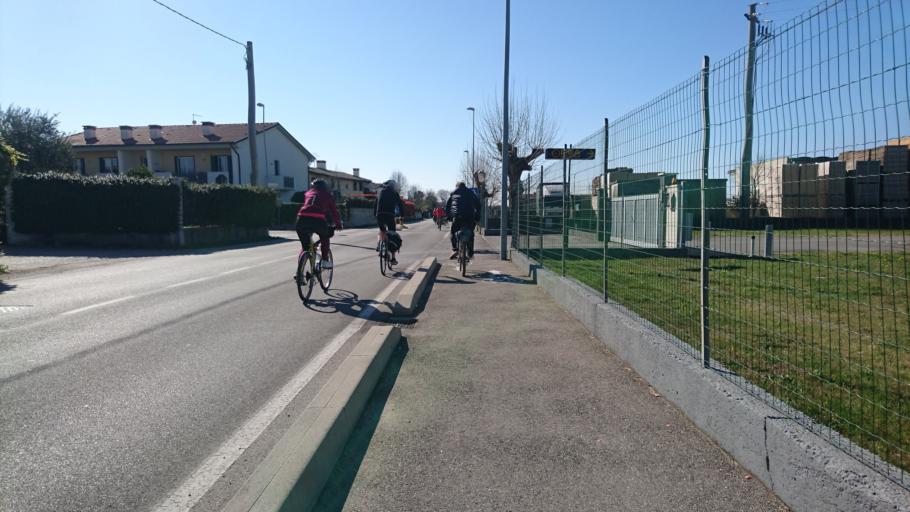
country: IT
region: Veneto
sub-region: Provincia di Vicenza
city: Bassano del Grappa
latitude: 45.7394
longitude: 11.7402
